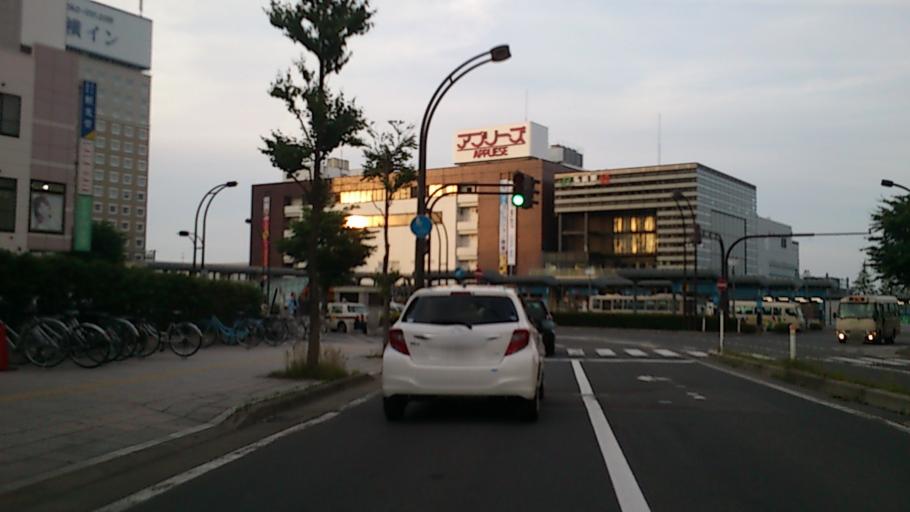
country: JP
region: Aomori
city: Hirosaki
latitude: 40.5981
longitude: 140.4835
